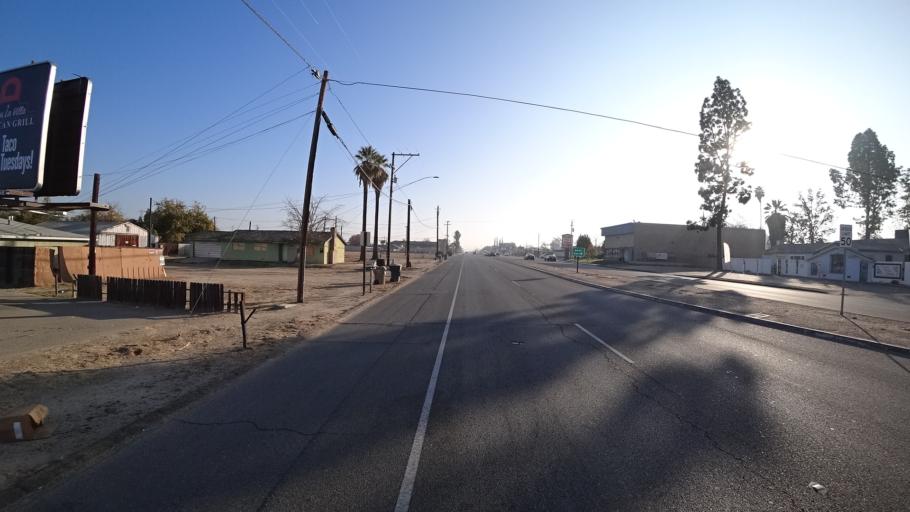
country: US
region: California
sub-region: Kern County
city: Greenacres
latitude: 35.3836
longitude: -119.1184
